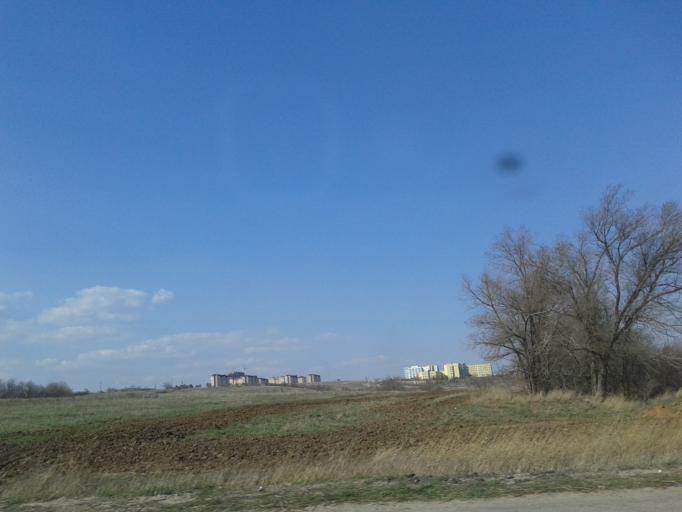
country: RU
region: Volgograd
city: Volgograd
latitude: 48.6308
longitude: 44.4141
